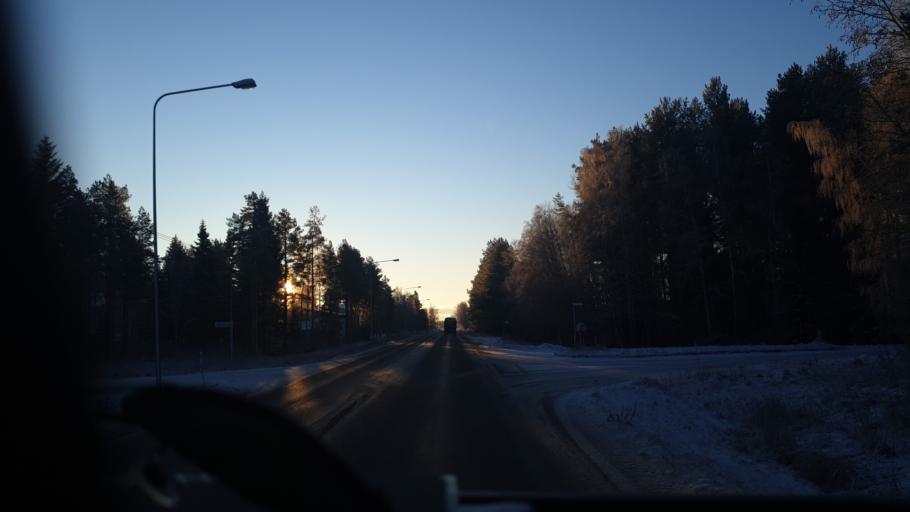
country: FI
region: Northern Ostrobothnia
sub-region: Ylivieska
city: Kalajoki
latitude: 64.2728
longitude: 23.9489
